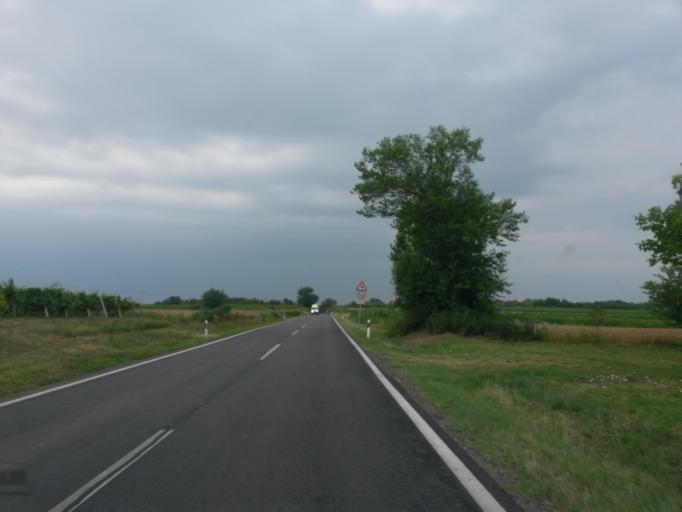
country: HR
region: Vukovarsko-Srijemska
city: Bapska
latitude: 45.2343
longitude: 19.2634
